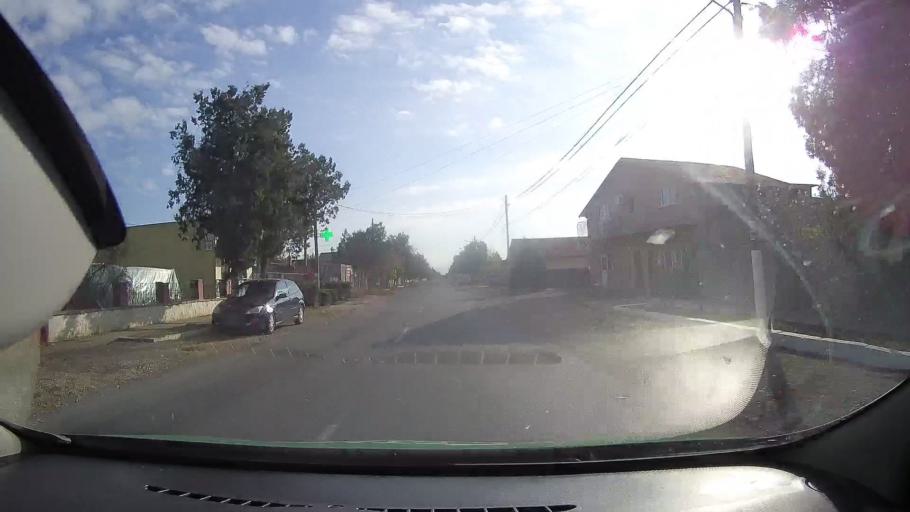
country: RO
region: Constanta
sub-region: Comuna Corbu
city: Corbu
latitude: 44.3916
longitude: 28.6620
